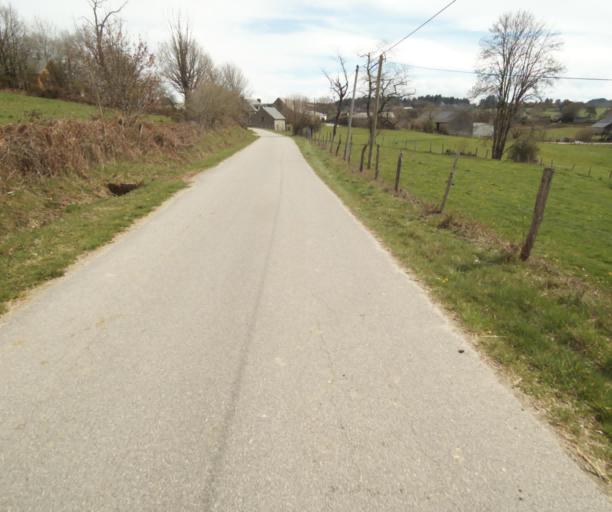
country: FR
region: Limousin
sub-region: Departement de la Correze
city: Correze
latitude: 45.3708
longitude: 1.9357
